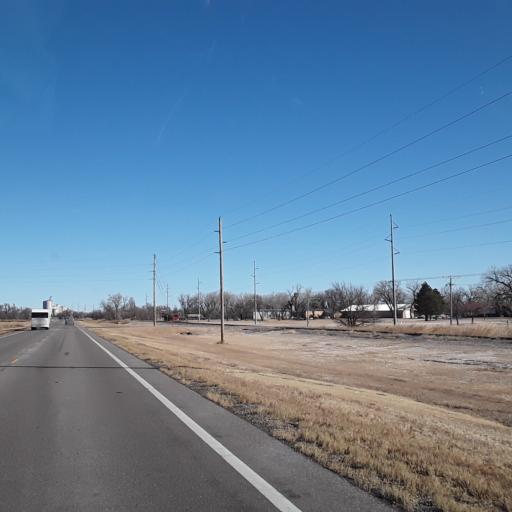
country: US
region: Kansas
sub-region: Pawnee County
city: Larned
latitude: 38.1641
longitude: -99.1155
